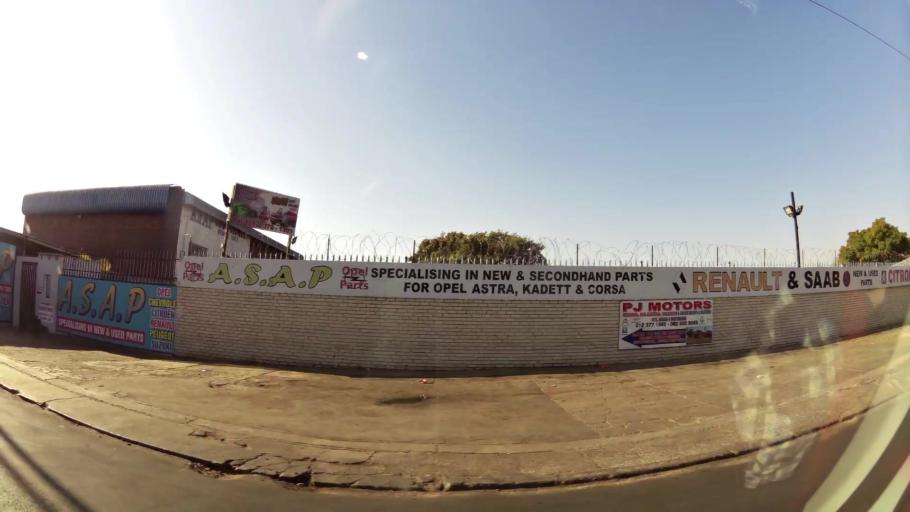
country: ZA
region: Gauteng
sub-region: City of Tshwane Metropolitan Municipality
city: Pretoria
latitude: -25.7238
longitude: 28.1604
